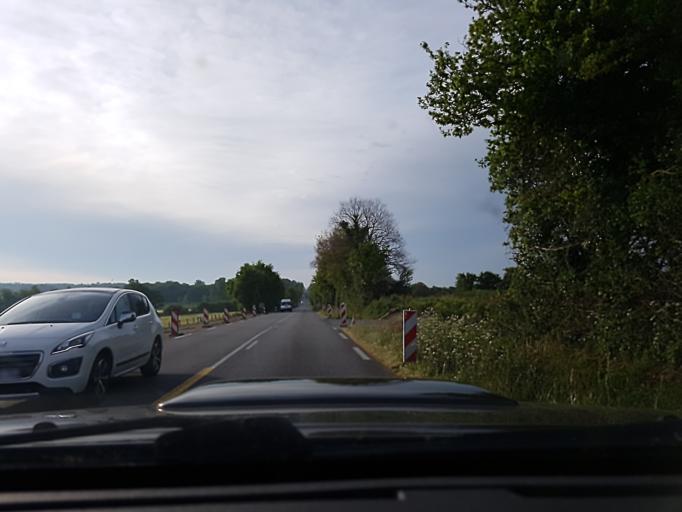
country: FR
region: Pays de la Loire
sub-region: Departement de la Vendee
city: Aizenay
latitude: 46.7570
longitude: -1.6410
